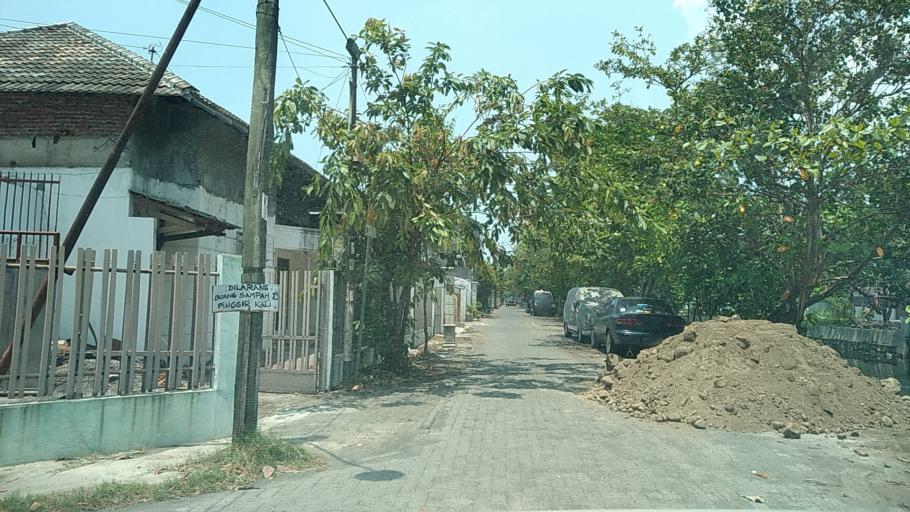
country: ID
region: Central Java
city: Semarang
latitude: -6.9727
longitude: 110.4379
